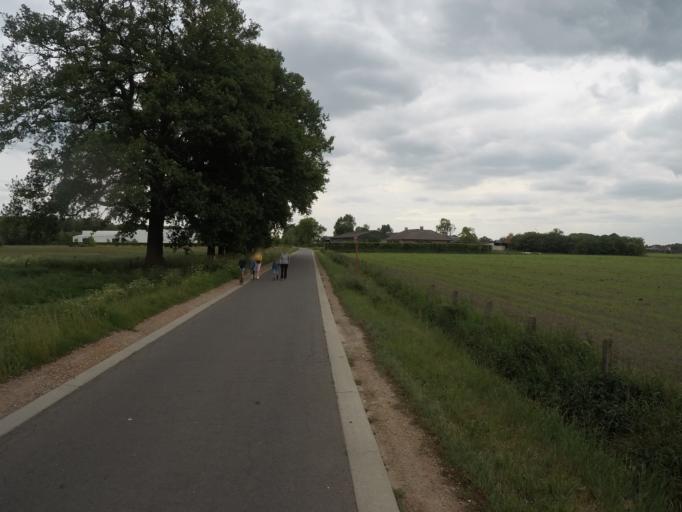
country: BE
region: Flanders
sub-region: Provincie Antwerpen
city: Oostmalle
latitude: 51.3069
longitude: 4.7069
